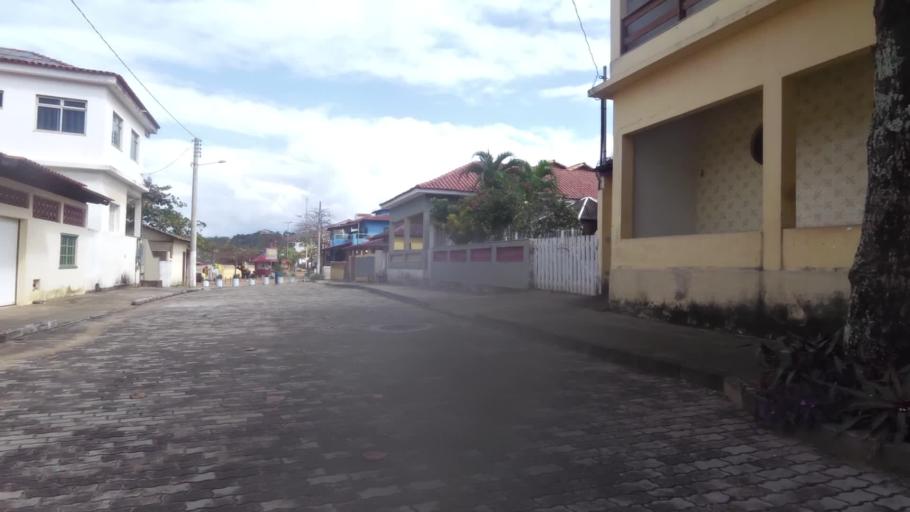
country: BR
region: Espirito Santo
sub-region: Piuma
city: Piuma
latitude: -20.8328
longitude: -40.6969
